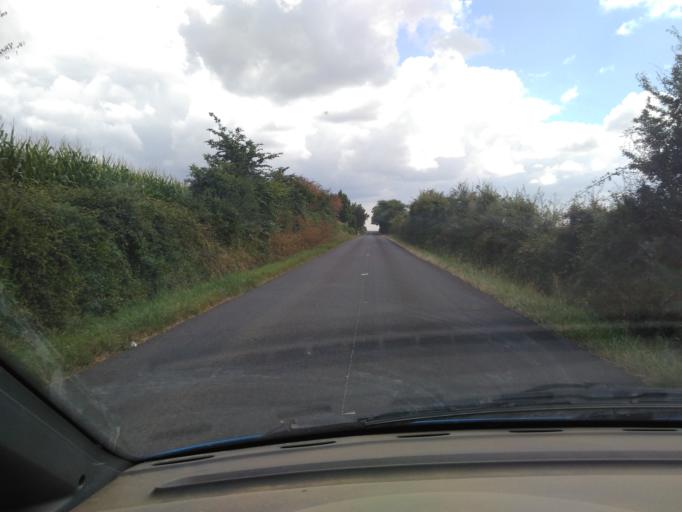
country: FR
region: Pays de la Loire
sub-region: Departement de la Vendee
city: Sainte-Hermine
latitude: 46.5539
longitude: -1.0297
